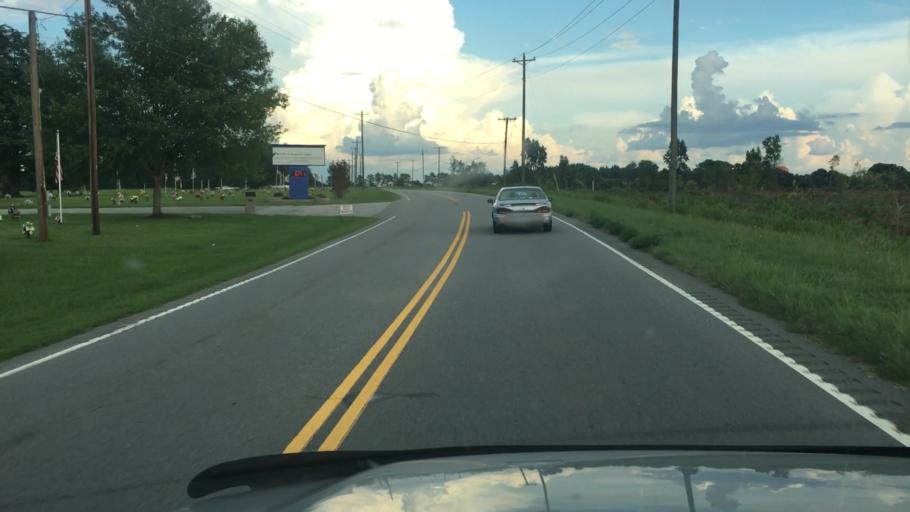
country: US
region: South Carolina
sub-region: Cherokee County
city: Gaffney
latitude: 35.1055
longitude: -81.6957
